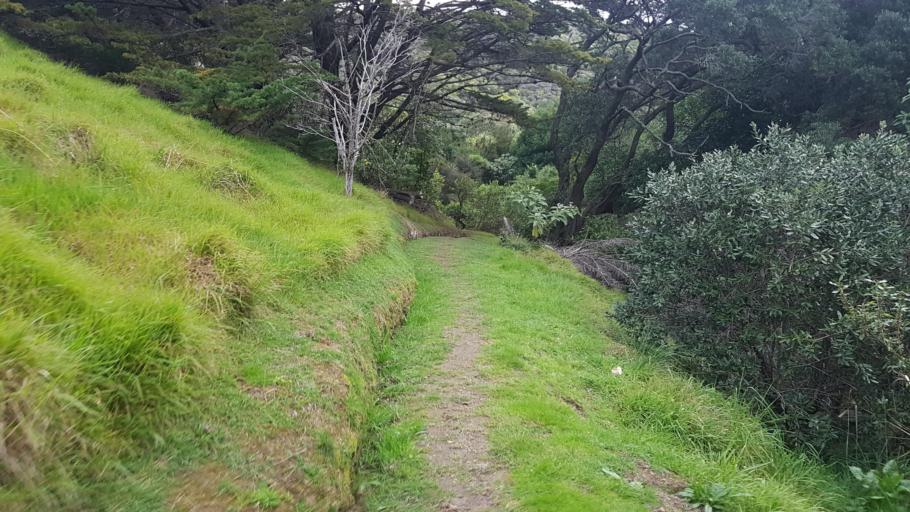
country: NZ
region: Auckland
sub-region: Auckland
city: Pakuranga
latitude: -36.7798
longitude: 174.9957
